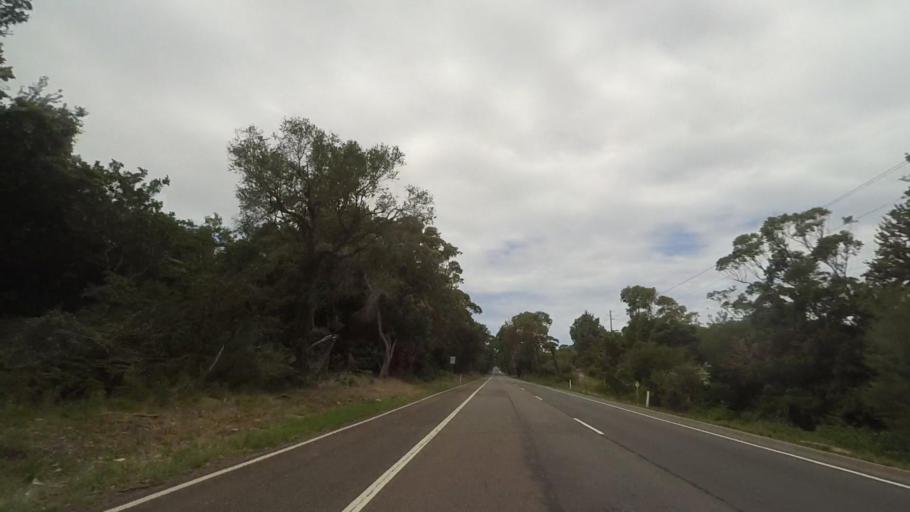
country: AU
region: New South Wales
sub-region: Wyong Shire
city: The Entrance
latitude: -33.3041
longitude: 151.5258
